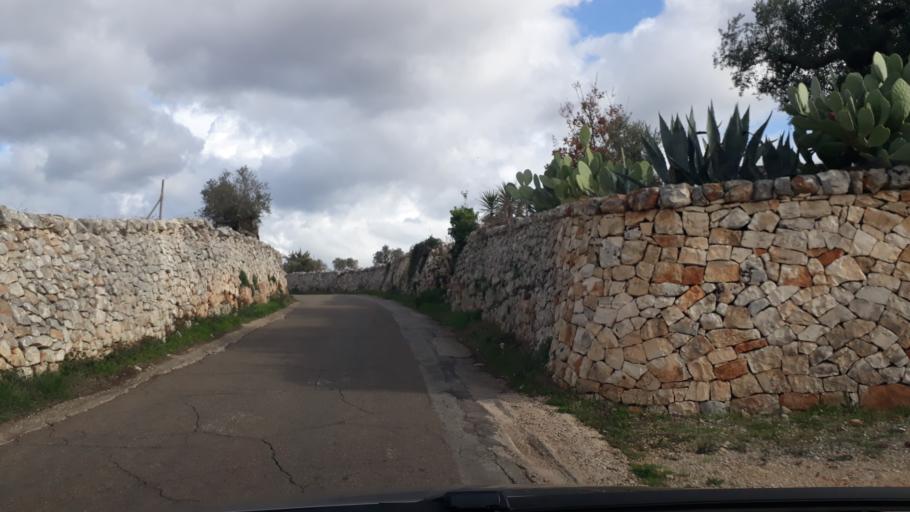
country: IT
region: Apulia
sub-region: Provincia di Brindisi
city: Cisternino
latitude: 40.7236
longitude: 17.4281
